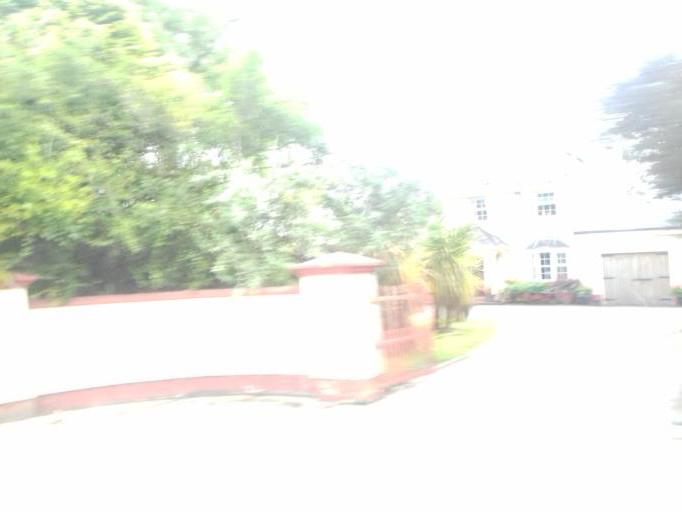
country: IE
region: Leinster
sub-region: Loch Garman
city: Loch Garman
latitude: 52.3401
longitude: -6.5783
